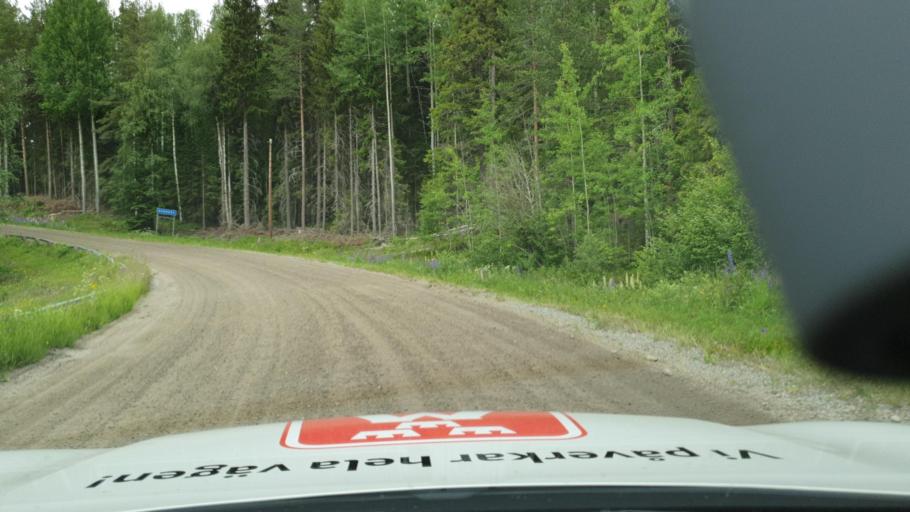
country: SE
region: Vaesterbotten
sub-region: Bjurholms Kommun
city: Bjurholm
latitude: 63.8372
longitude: 18.9998
